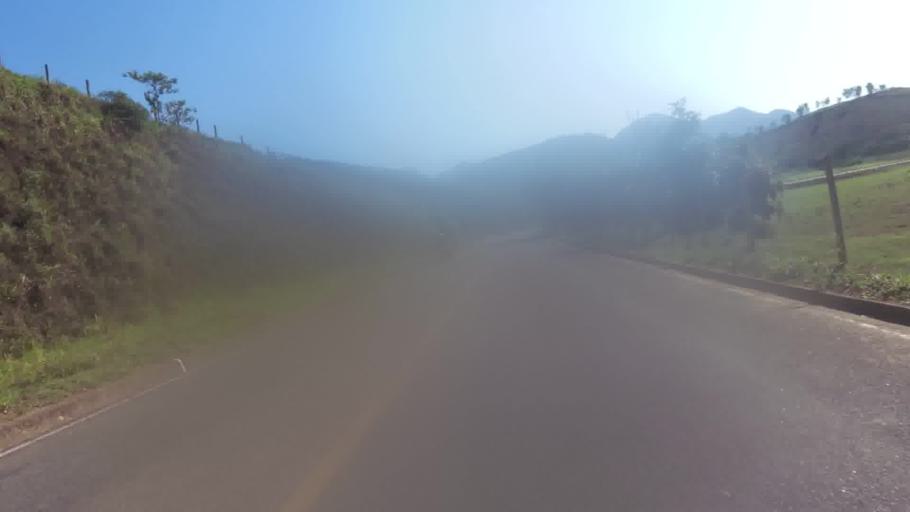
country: BR
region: Espirito Santo
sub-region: Alfredo Chaves
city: Alfredo Chaves
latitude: -20.6571
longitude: -40.7613
